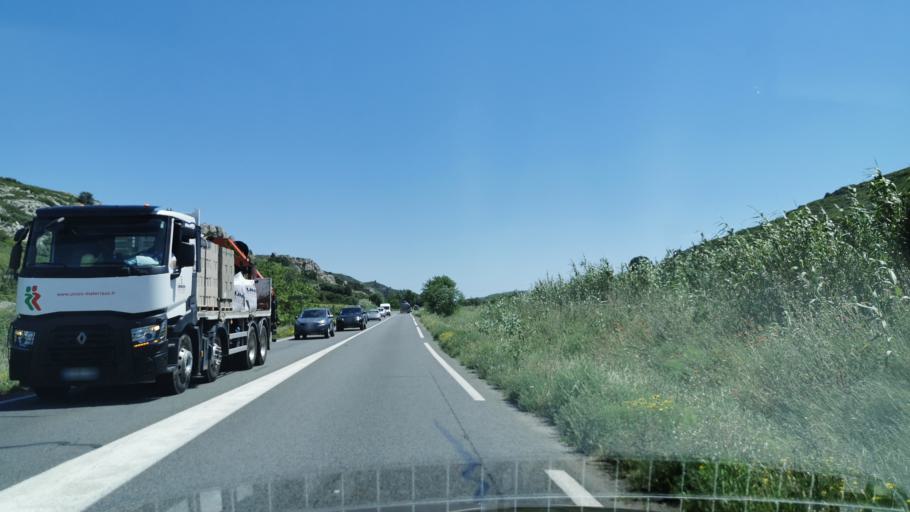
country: FR
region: Languedoc-Roussillon
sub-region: Departement de l'Aude
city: Nevian
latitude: 43.2063
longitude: 2.8854
